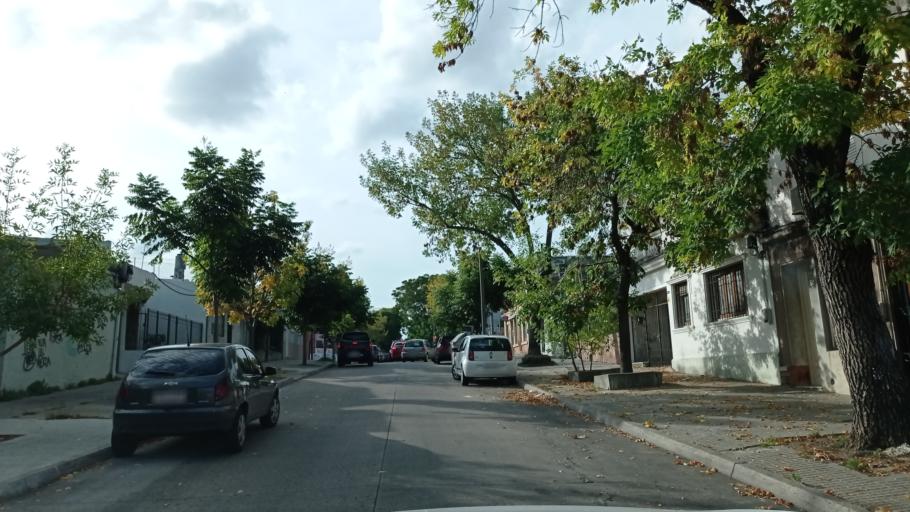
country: UY
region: Montevideo
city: Montevideo
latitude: -34.8862
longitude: -56.1751
